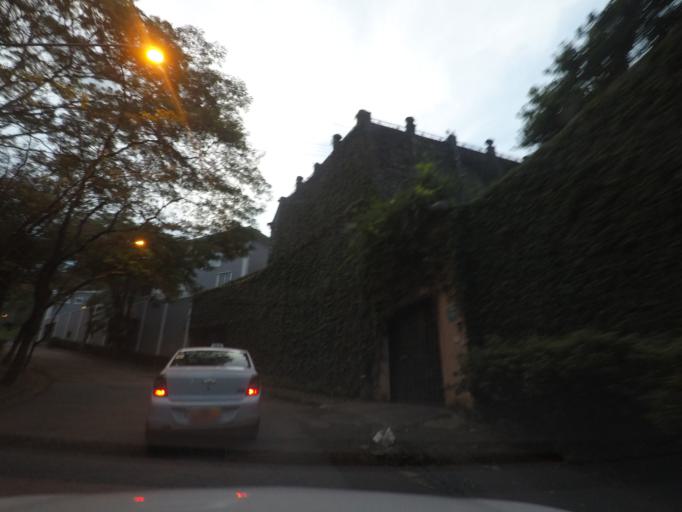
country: BR
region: Sao Paulo
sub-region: Taboao Da Serra
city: Taboao da Serra
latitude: -23.6143
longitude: -46.7109
